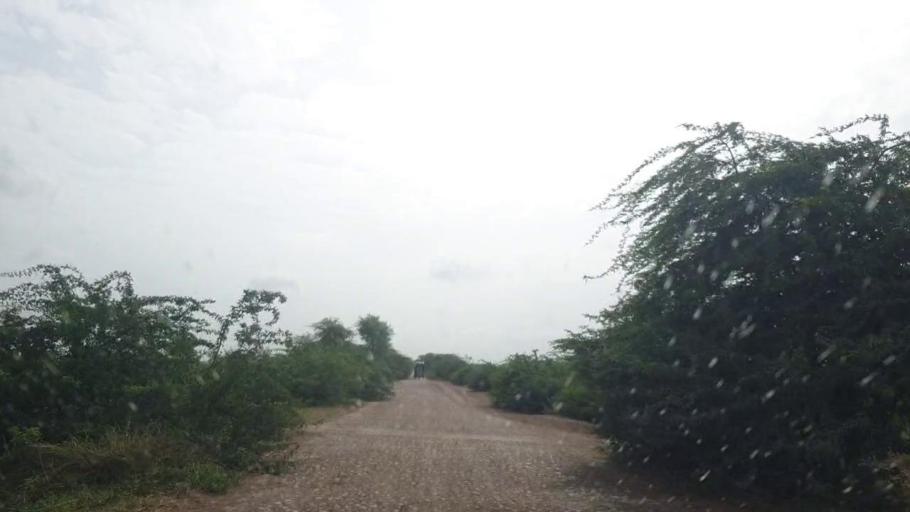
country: PK
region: Sindh
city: Tando Bago
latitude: 24.7929
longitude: 68.9828
